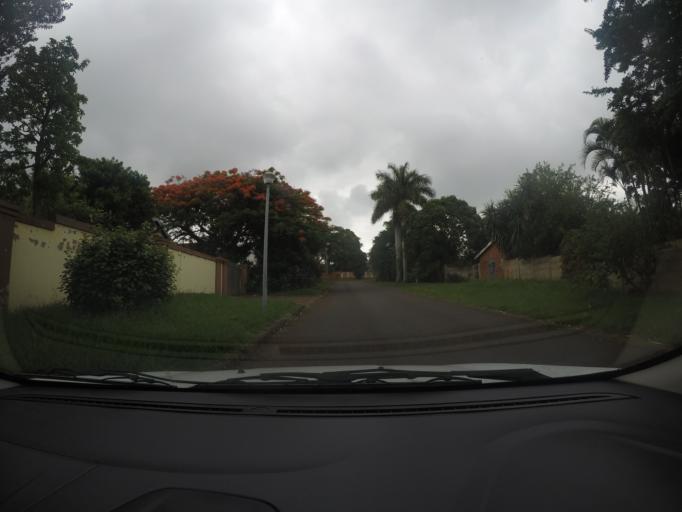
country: ZA
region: KwaZulu-Natal
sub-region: uThungulu District Municipality
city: Empangeni
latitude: -28.7635
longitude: 31.8998
